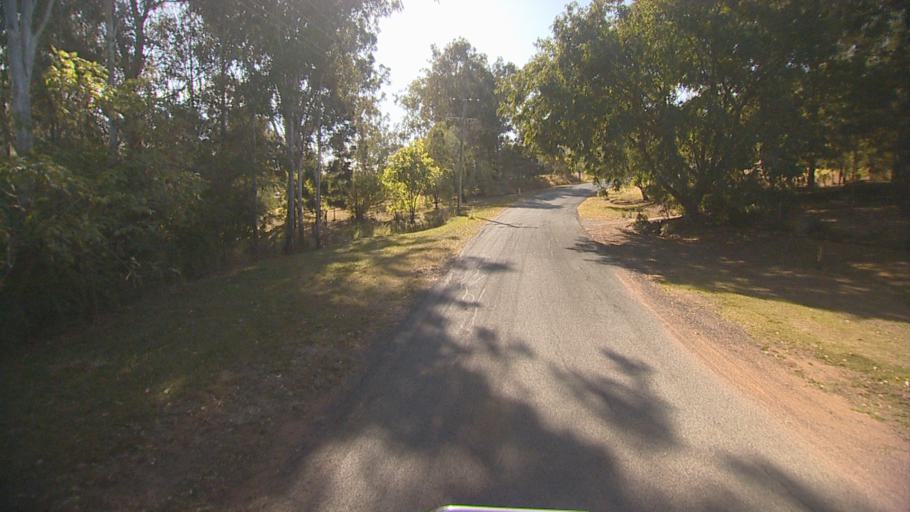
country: AU
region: Queensland
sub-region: Logan
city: Cedar Vale
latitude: -27.8522
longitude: 152.9867
